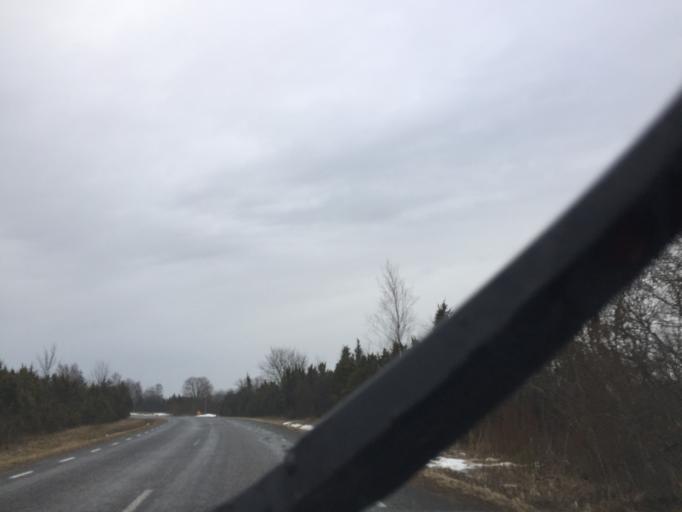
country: EE
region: Saare
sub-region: Orissaare vald
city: Orissaare
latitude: 58.5753
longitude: 23.0290
